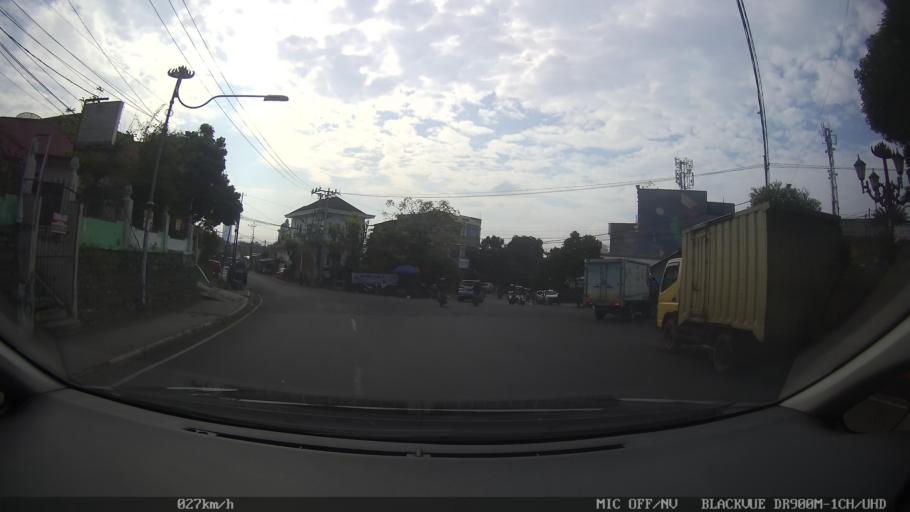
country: ID
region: Lampung
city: Bandarlampung
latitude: -5.4430
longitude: 105.2689
